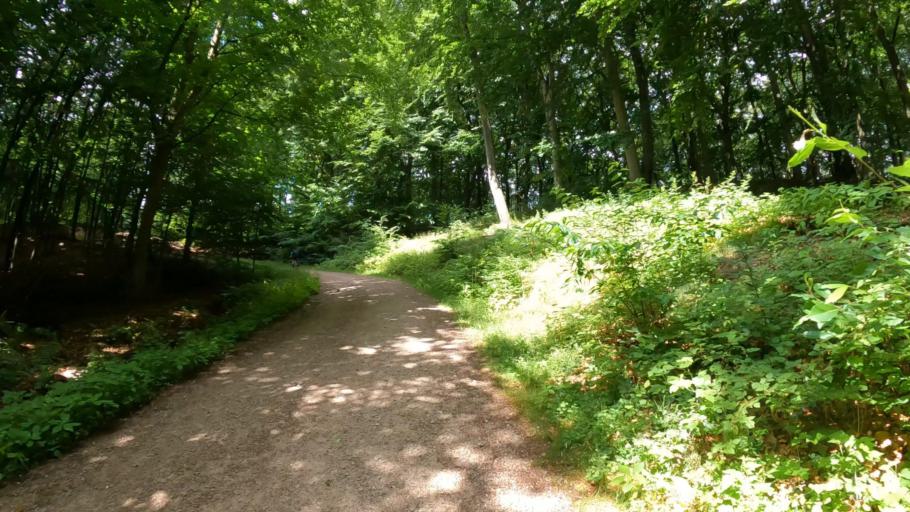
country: DE
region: Hamburg
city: Harburg
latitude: 53.4563
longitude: 9.9245
